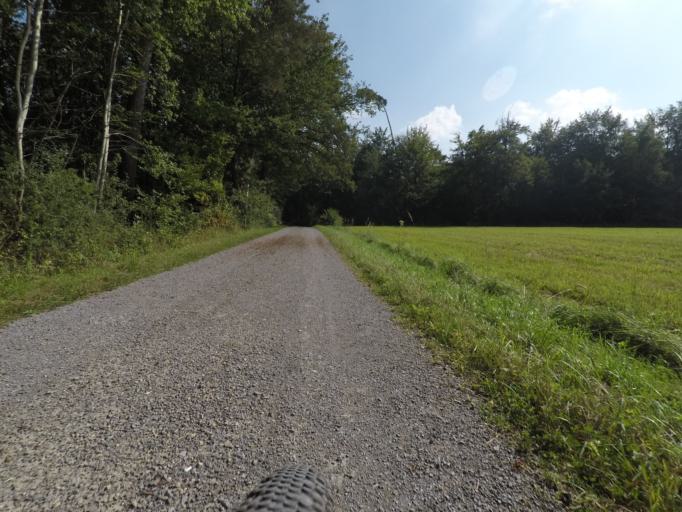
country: DE
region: Baden-Wuerttemberg
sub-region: Regierungsbezirk Stuttgart
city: Steinenbronn
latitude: 48.6853
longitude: 9.1089
